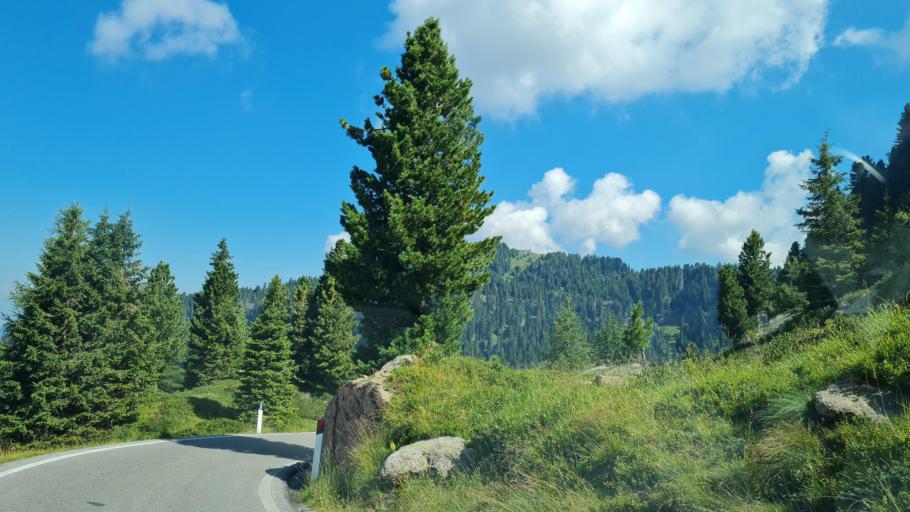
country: IT
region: Trentino-Alto Adige
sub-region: Provincia di Trento
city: Palu del Fersina
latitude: 46.1750
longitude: 11.4392
